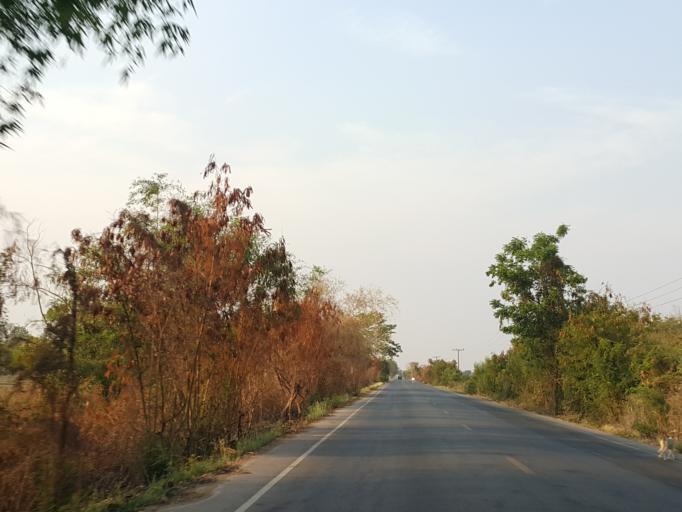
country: TH
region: Sukhothai
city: Si Samrong
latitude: 17.2153
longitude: 99.9497
